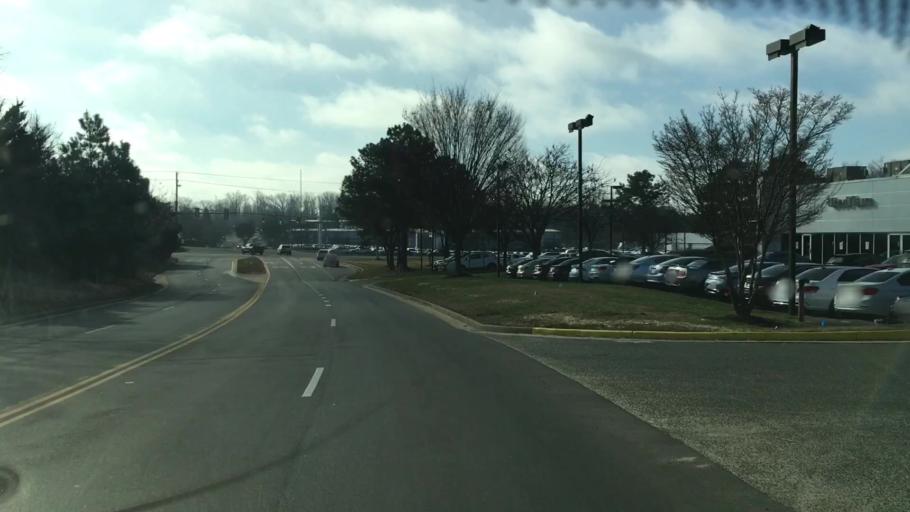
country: US
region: Virginia
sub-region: Chesterfield County
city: Bon Air
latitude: 37.5060
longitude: -77.6180
